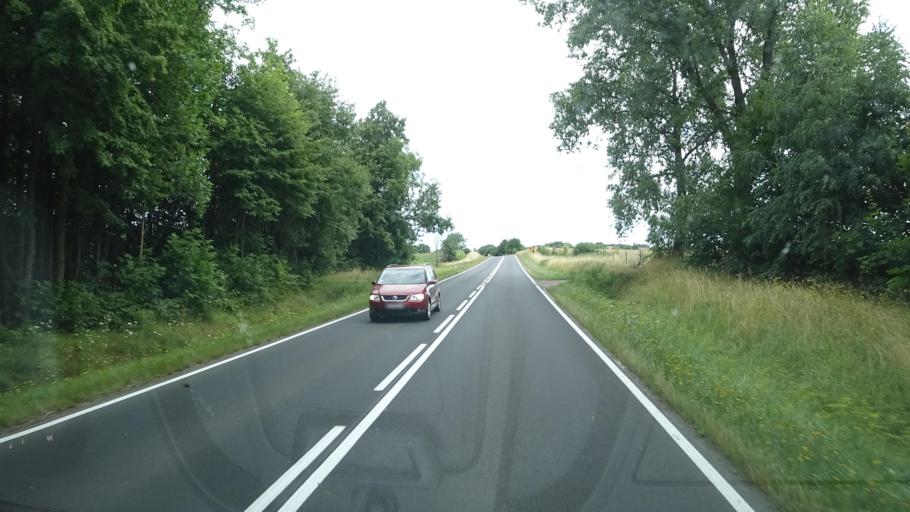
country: PL
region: Warmian-Masurian Voivodeship
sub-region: Powiat elcki
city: Elk
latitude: 53.7968
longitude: 22.2317
